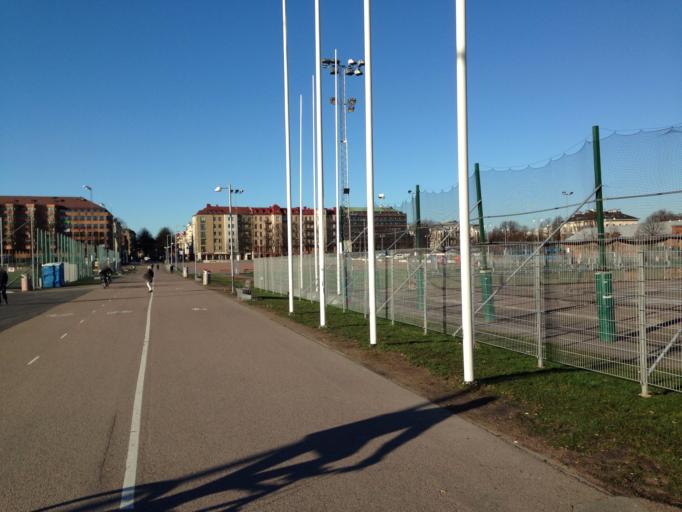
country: SE
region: Vaestra Goetaland
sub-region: Goteborg
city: Goeteborg
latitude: 57.7028
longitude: 11.9795
